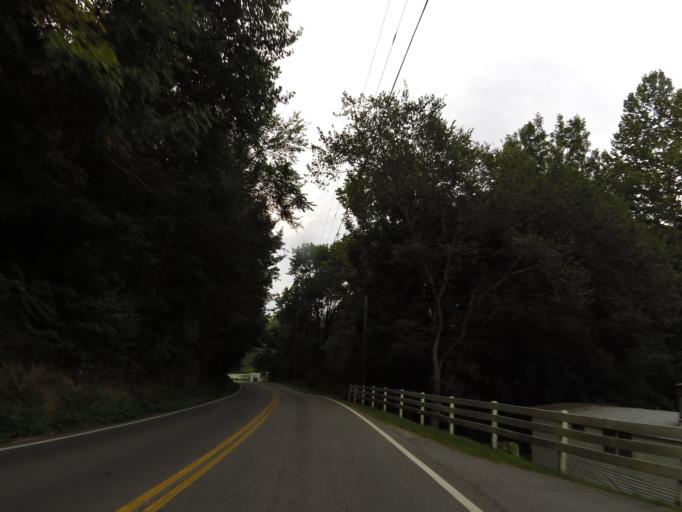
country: US
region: Tennessee
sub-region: Anderson County
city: Rocky Top
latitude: 36.1861
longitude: -84.1846
